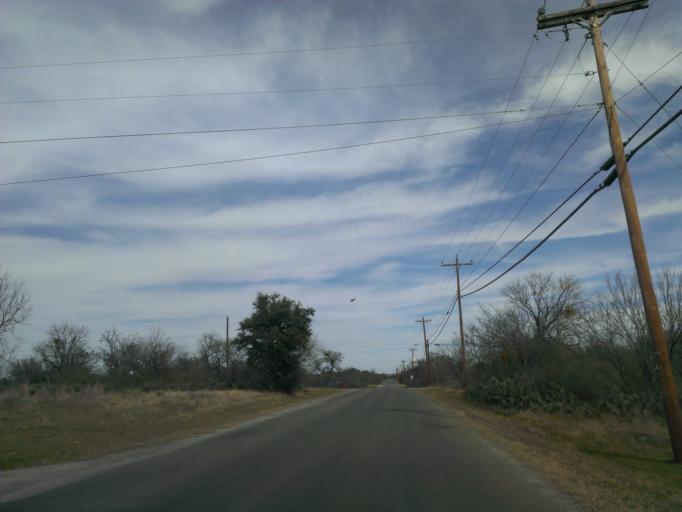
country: US
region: Texas
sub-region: Burnet County
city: Granite Shoals
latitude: 30.5792
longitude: -98.3934
